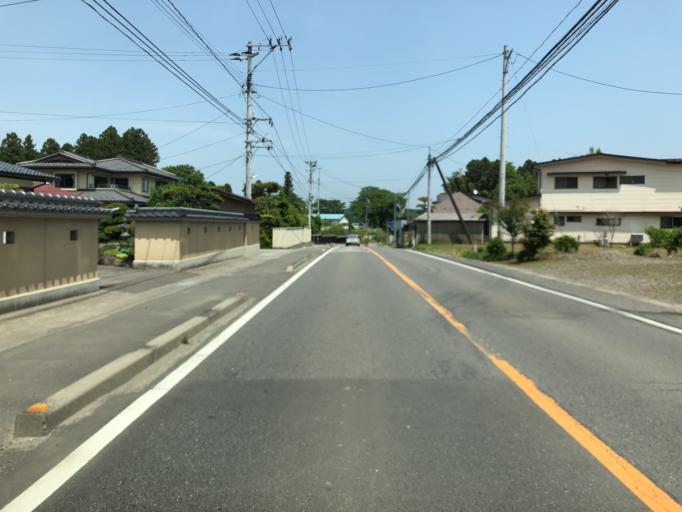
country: JP
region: Fukushima
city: Ishikawa
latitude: 37.1419
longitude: 140.3981
